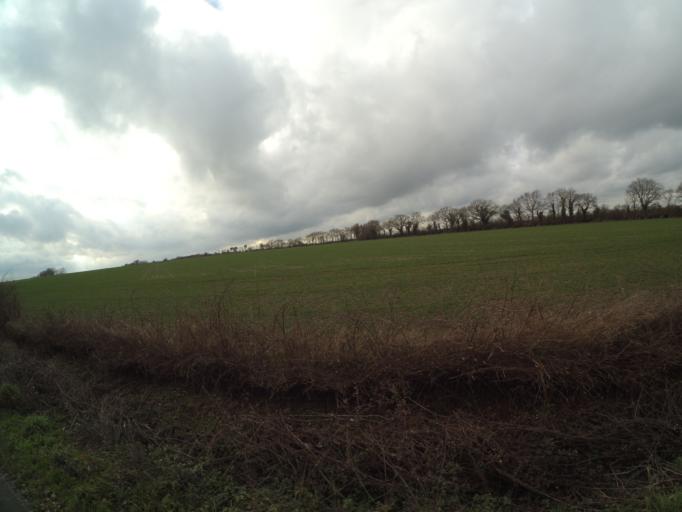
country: FR
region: Pays de la Loire
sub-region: Departement de la Vendee
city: La Bernardiere
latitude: 47.0255
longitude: -1.2924
